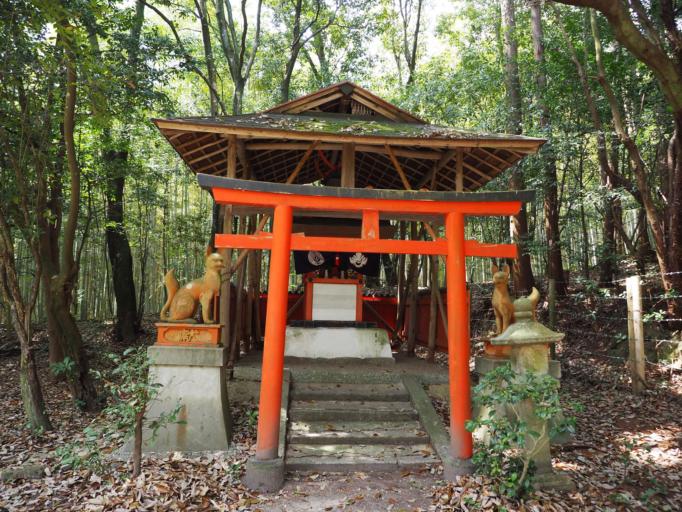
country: JP
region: Nara
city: Nara-shi
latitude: 34.6430
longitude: 135.8443
